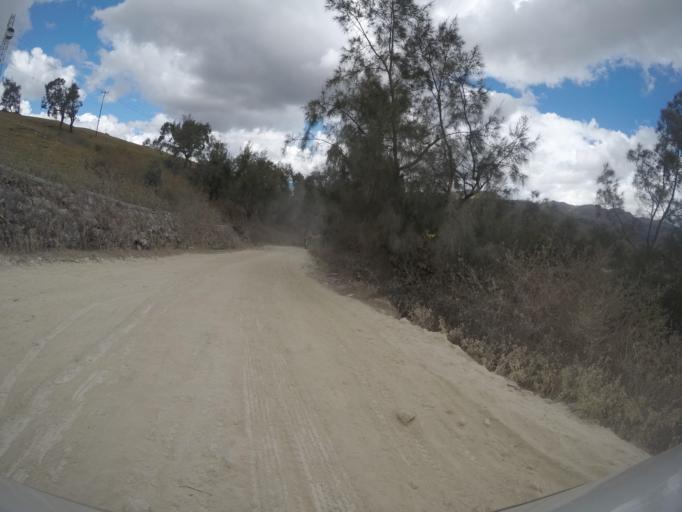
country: TL
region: Baucau
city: Baucau
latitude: -8.4992
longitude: 126.6772
